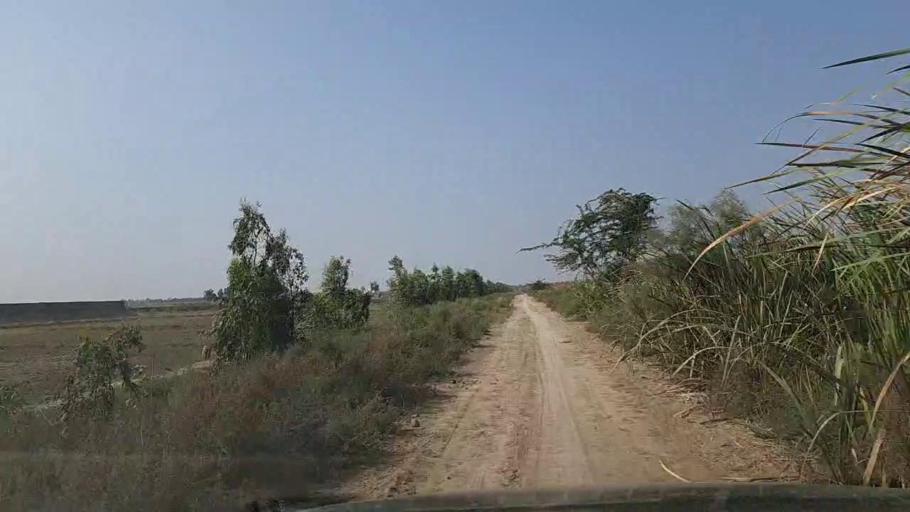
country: PK
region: Sindh
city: Gharo
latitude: 24.7293
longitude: 67.7219
